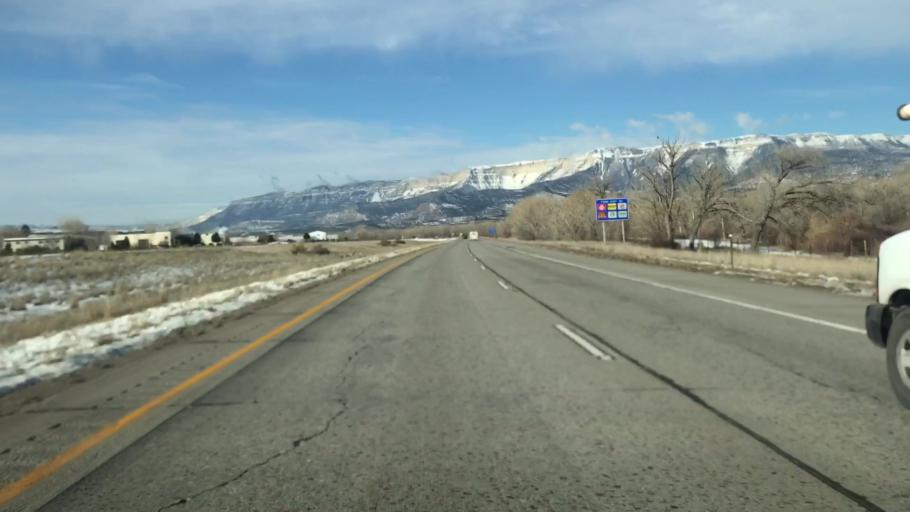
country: US
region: Colorado
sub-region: Garfield County
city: Rifle
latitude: 39.5253
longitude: -107.7578
